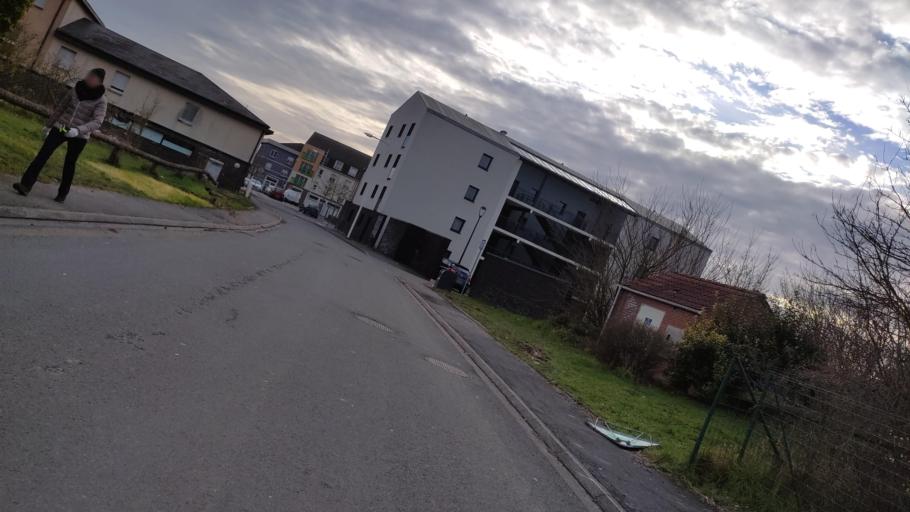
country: FR
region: Nord-Pas-de-Calais
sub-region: Departement du Pas-de-Calais
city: Anzin-Saint-Aubin
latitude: 50.3040
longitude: 2.7389
